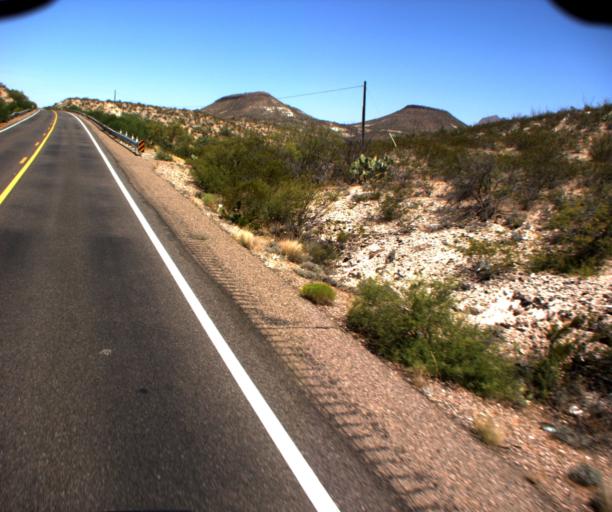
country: US
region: Arizona
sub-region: Gila County
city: Peridot
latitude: 33.2784
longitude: -110.3320
